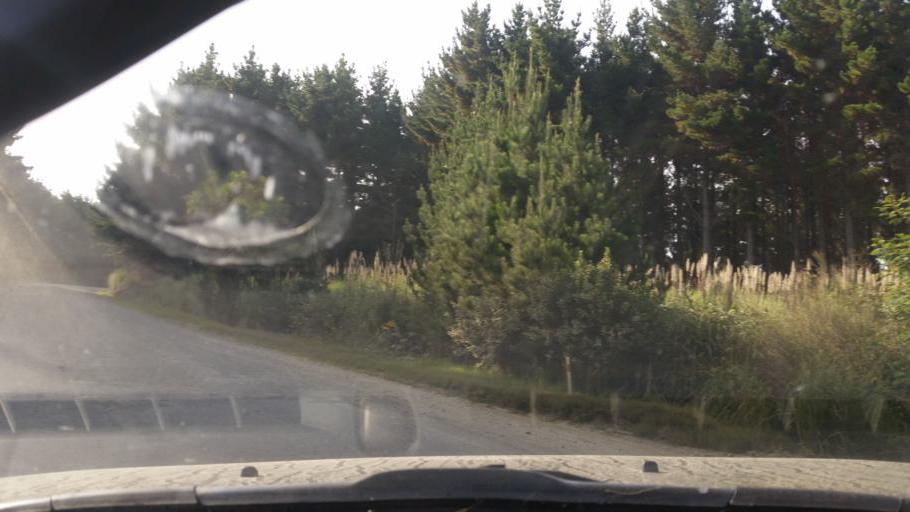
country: NZ
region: Northland
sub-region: Kaipara District
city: Dargaville
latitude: -36.2353
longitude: 174.0453
